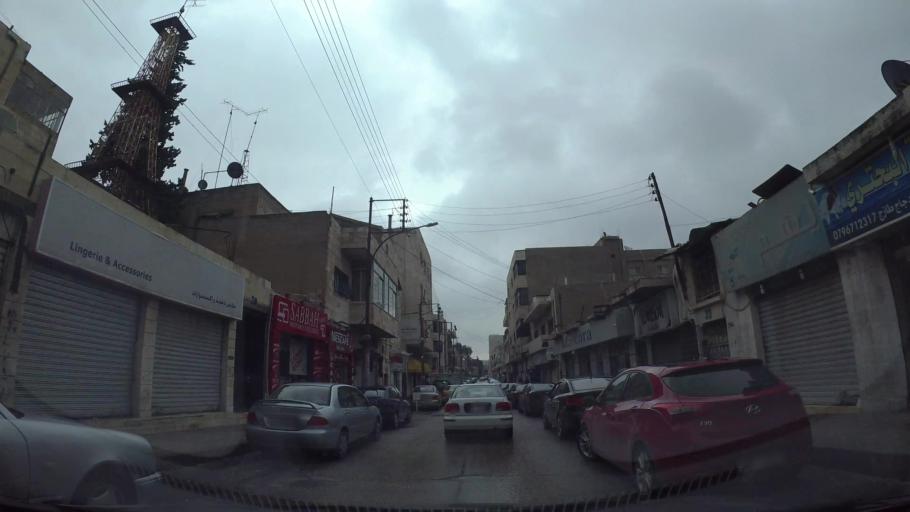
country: JO
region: Amman
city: Amman
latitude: 31.9484
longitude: 35.9191
